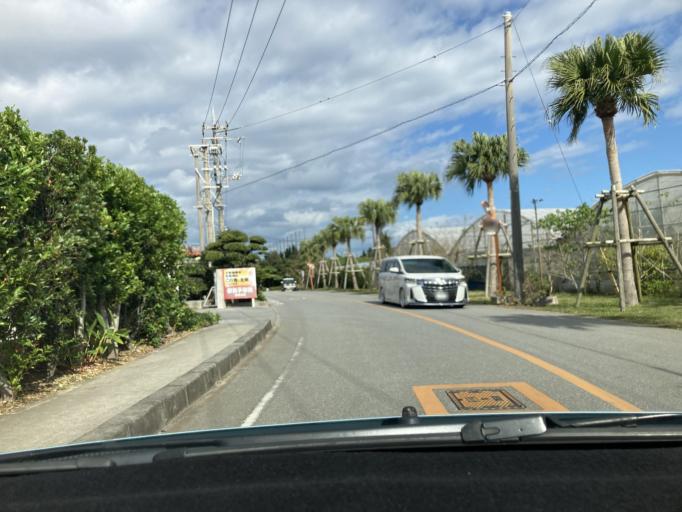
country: JP
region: Okinawa
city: Ishikawa
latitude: 26.4323
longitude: 127.7193
